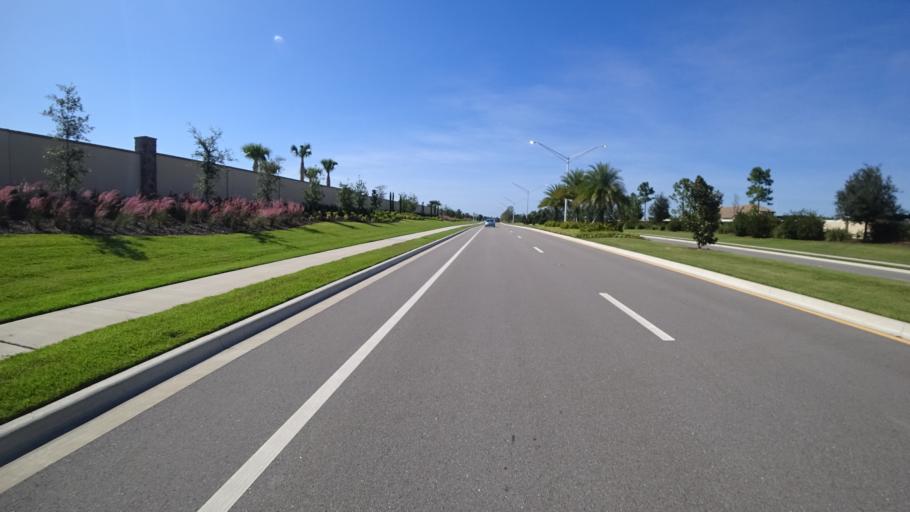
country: US
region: Florida
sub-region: Sarasota County
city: The Meadows
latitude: 27.4012
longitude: -82.3706
